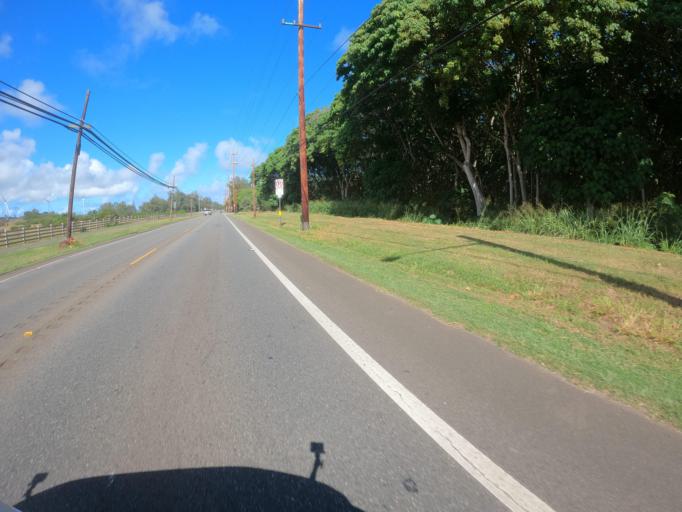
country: US
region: Hawaii
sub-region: Honolulu County
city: La'ie
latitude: 21.6597
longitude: -157.9325
